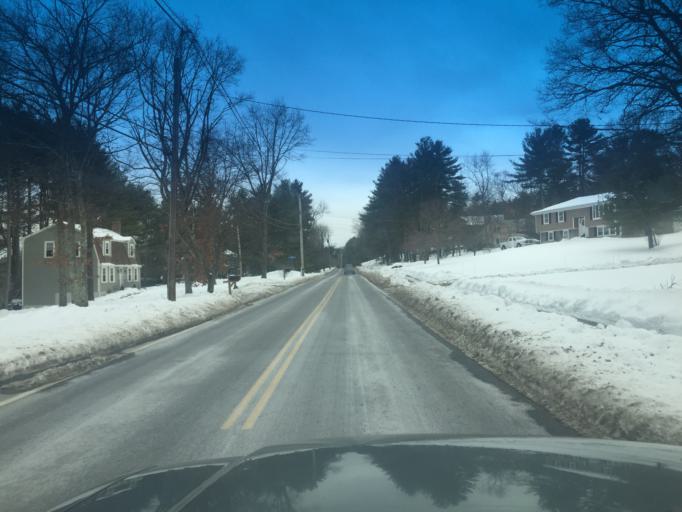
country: US
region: Massachusetts
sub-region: Norfolk County
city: Norfolk
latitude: 42.1066
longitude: -71.2830
